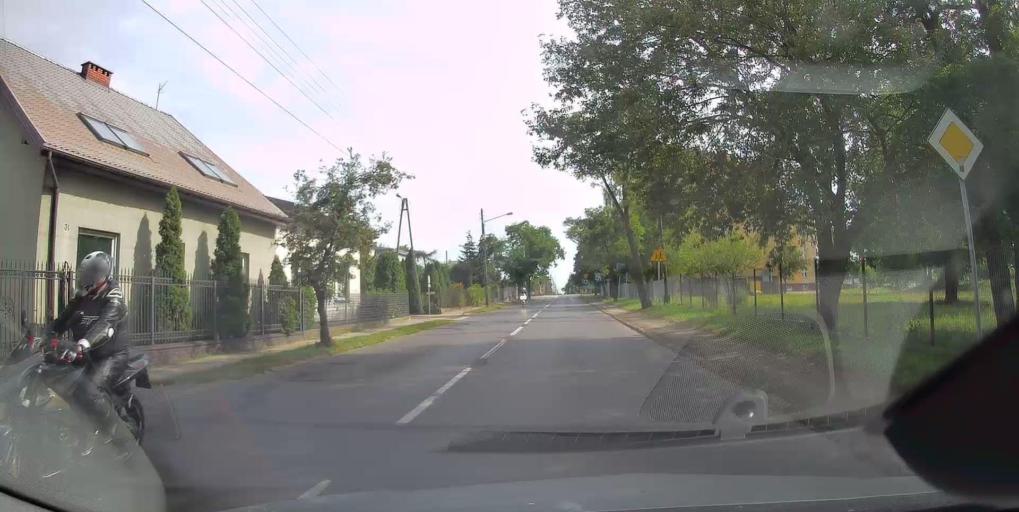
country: PL
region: Lodz Voivodeship
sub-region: Powiat tomaszowski
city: Tomaszow Mazowiecki
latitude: 51.5317
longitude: 19.9966
